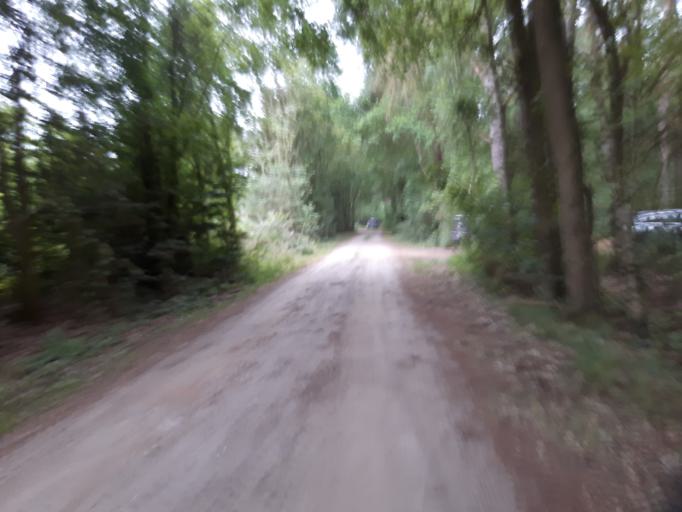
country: DE
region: Lower Saxony
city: Garstedt
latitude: 53.3127
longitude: 10.1960
